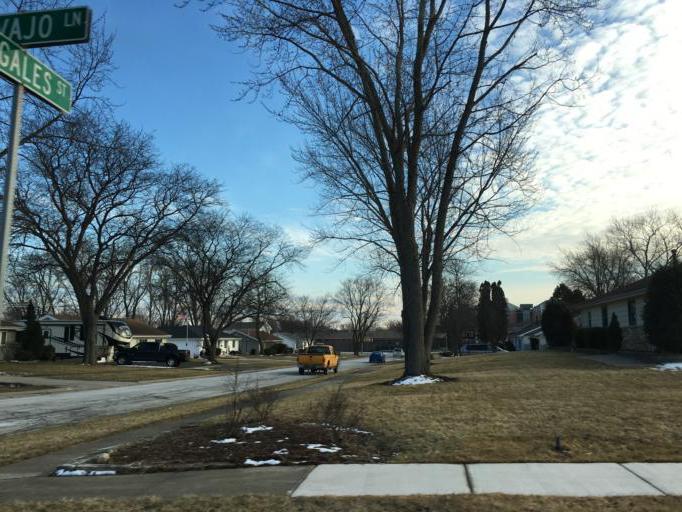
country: US
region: Illinois
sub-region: Cook County
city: Schaumburg
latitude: 42.0326
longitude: -88.0862
